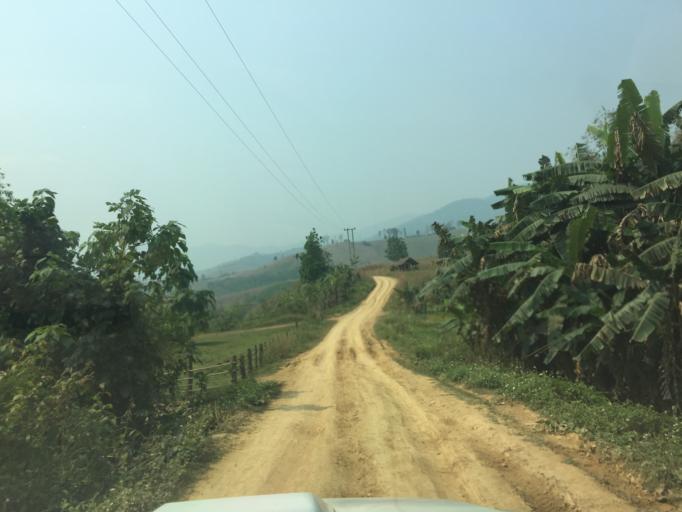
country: TH
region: Phayao
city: Phu Sang
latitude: 19.5938
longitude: 100.5282
